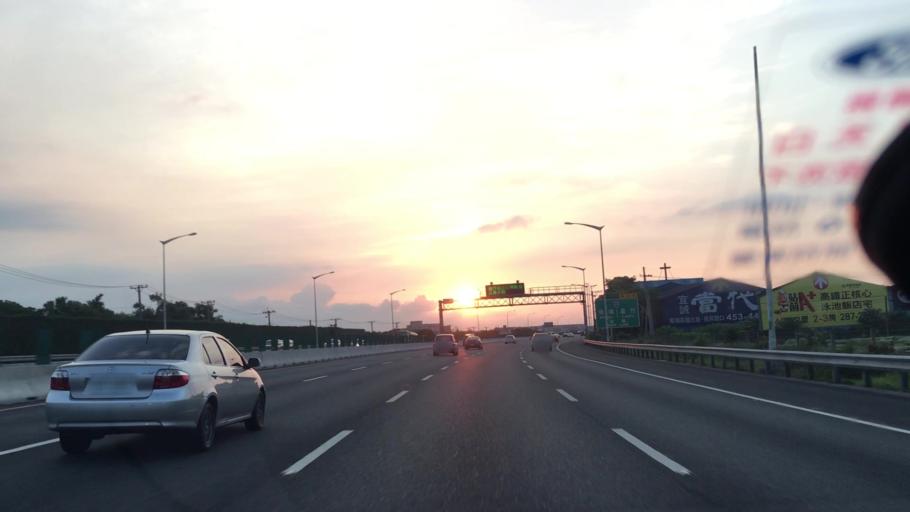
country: TW
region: Taiwan
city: Taoyuan City
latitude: 25.0281
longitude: 121.2524
